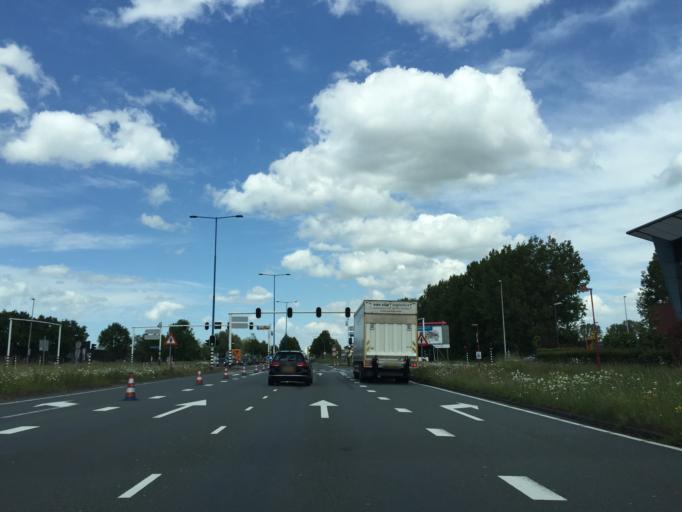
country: NL
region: South Holland
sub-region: Gemeente Zoetermeer
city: Zoetermeer
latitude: 52.0552
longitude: 4.5223
